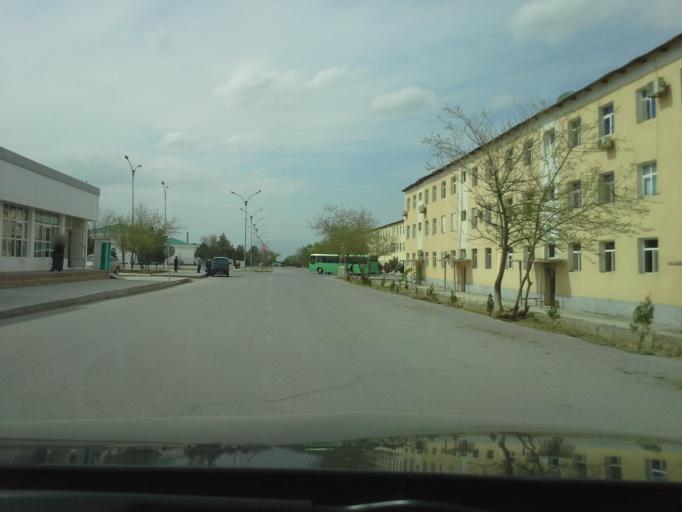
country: TM
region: Ahal
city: Abadan
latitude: 38.0579
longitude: 58.1511
